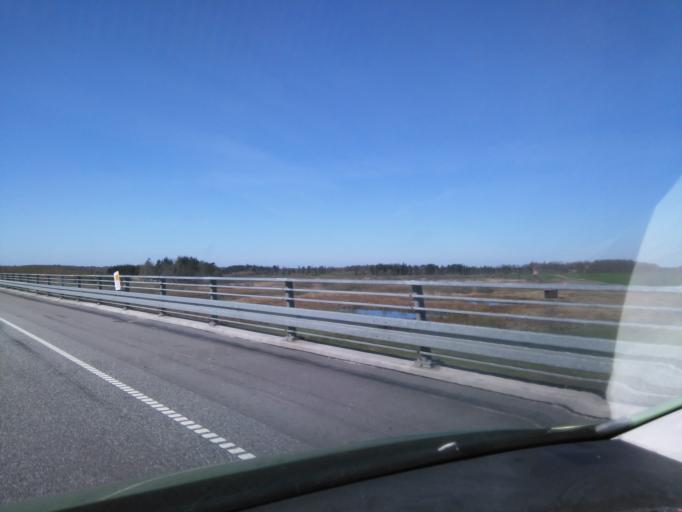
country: DK
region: South Denmark
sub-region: Vejle Kommune
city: Give
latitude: 55.8062
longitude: 9.2233
